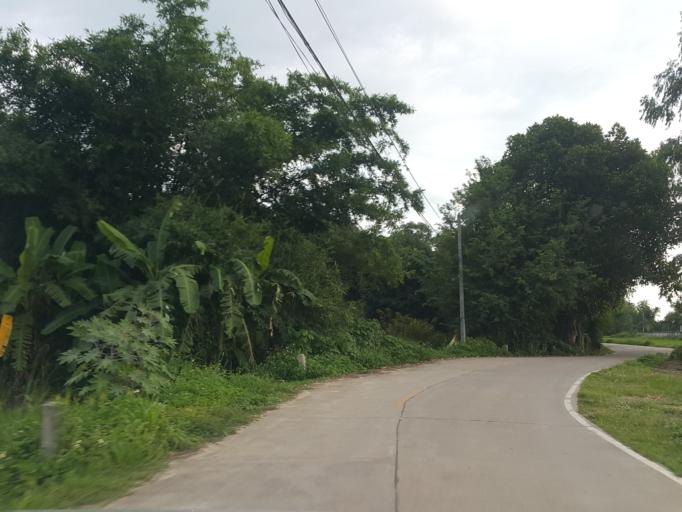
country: TH
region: Chiang Mai
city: San Sai
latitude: 18.8847
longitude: 99.0838
